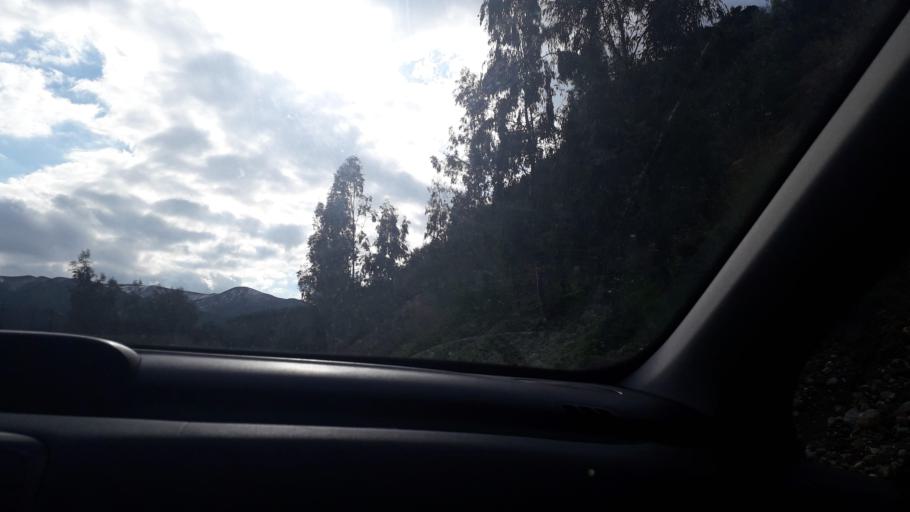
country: GR
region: Crete
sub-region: Nomos Rethymnis
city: Agia Foteini
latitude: 35.2858
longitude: 24.5637
